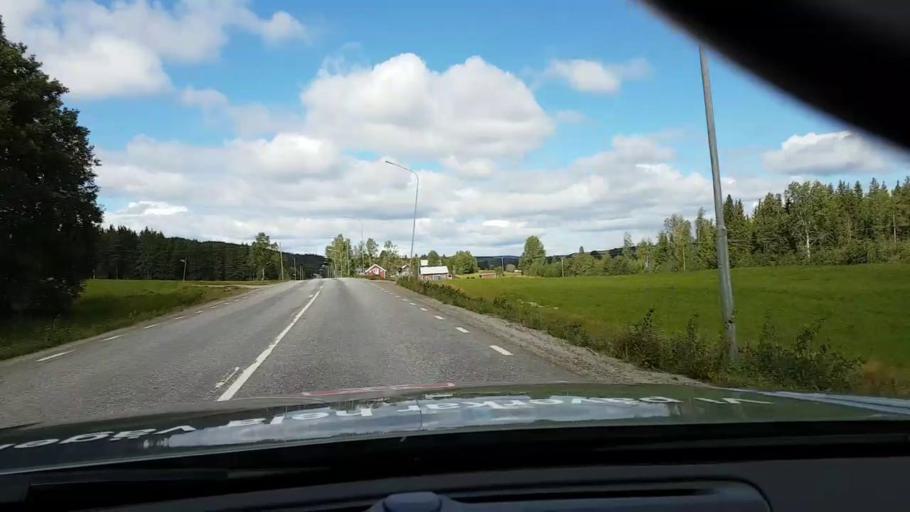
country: SE
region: Vaesternorrland
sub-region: OErnskoeldsviks Kommun
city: Bredbyn
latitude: 63.4788
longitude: 18.0929
